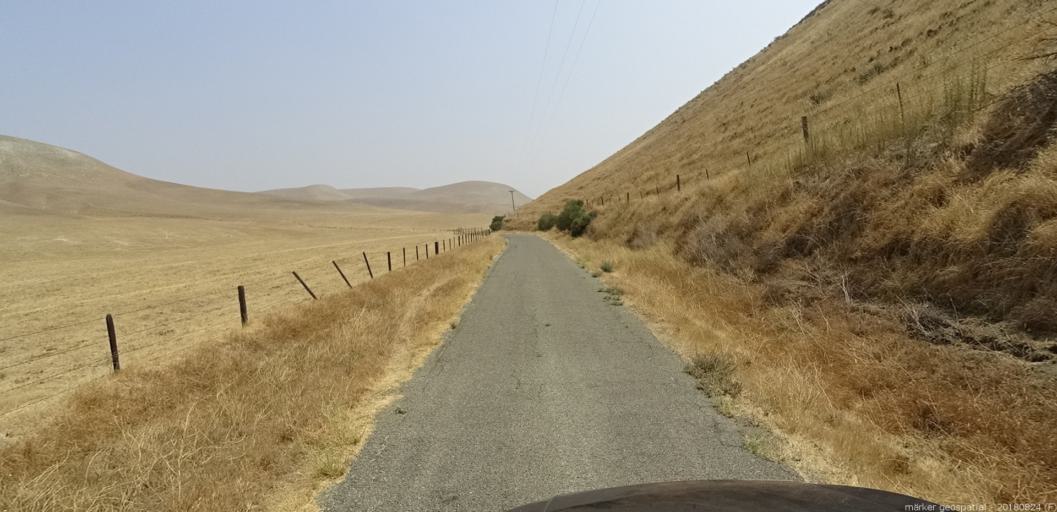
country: US
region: California
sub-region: Monterey County
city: King City
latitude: 36.1993
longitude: -121.0087
